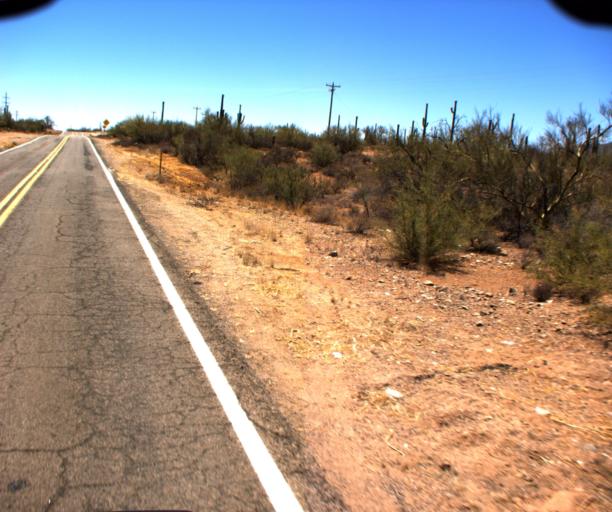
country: US
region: Arizona
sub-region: Pima County
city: Sells
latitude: 32.1545
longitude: -112.1072
